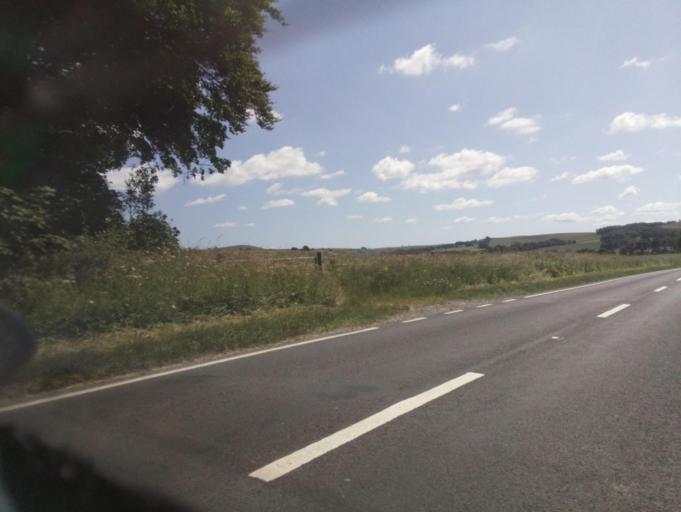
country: GB
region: England
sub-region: Derbyshire
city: Buxton
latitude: 53.2325
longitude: -1.8833
